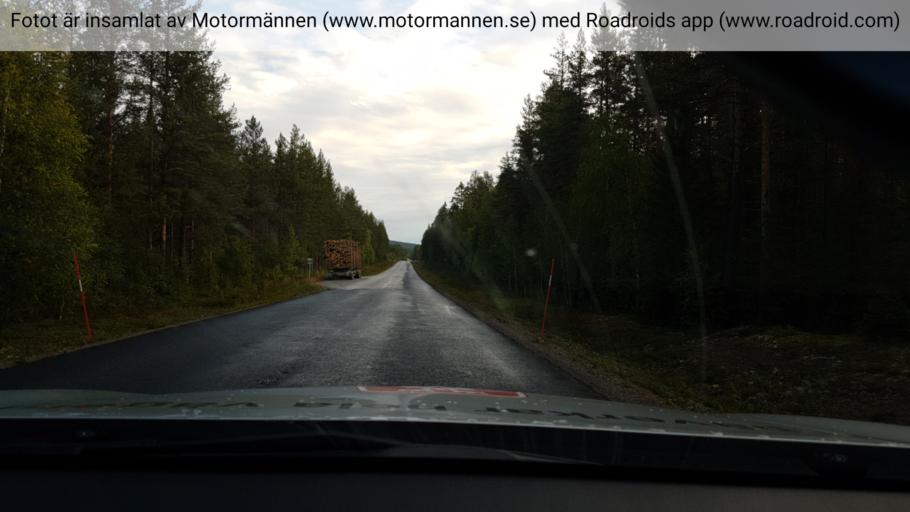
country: SE
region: Vaesterbotten
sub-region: Vindelns Kommun
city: Vindeln
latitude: 64.2283
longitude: 19.7777
